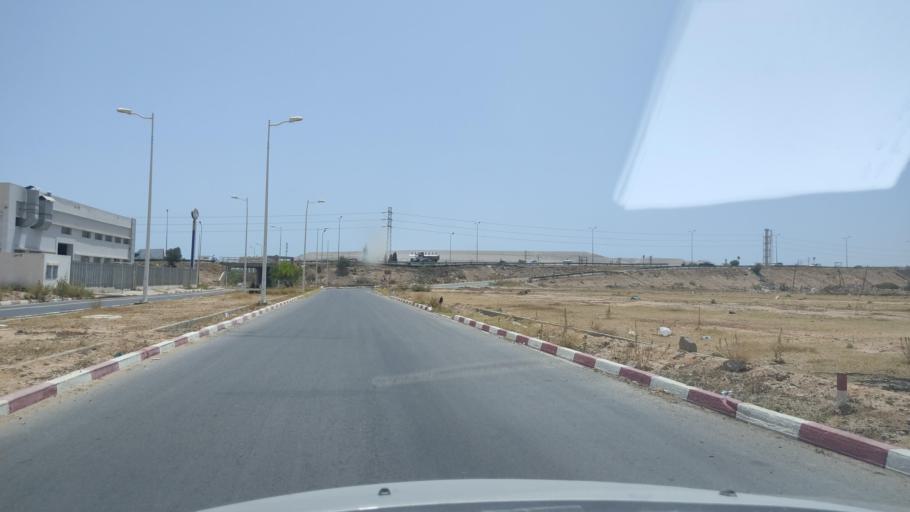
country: TN
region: Safaqis
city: Sfax
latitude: 34.7081
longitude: 10.7208
